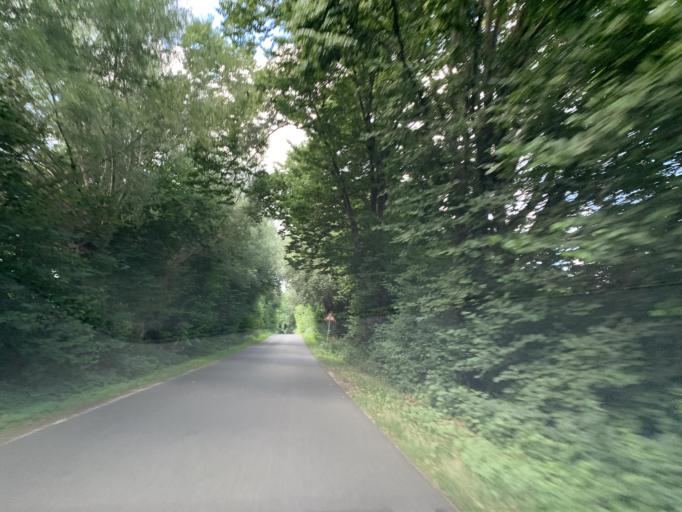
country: DE
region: Mecklenburg-Vorpommern
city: Carpin
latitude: 53.3698
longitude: 13.2566
